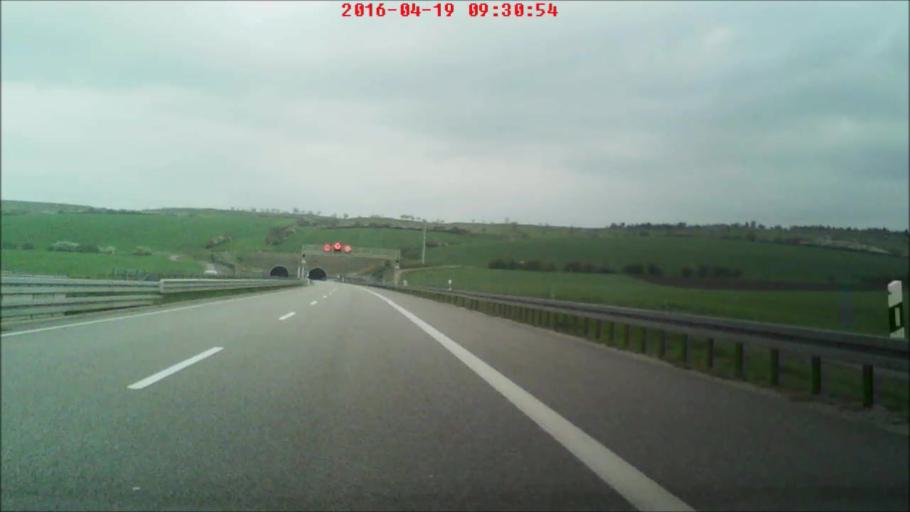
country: DE
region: Thuringia
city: Hemleben
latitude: 51.2632
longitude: 11.2089
